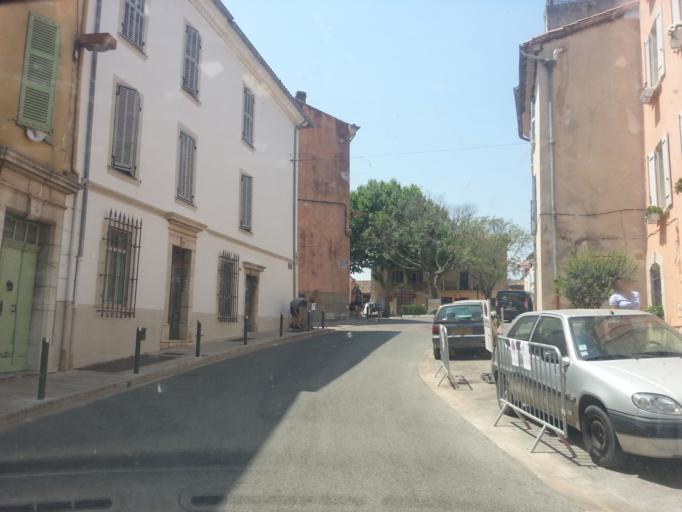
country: FR
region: Provence-Alpes-Cote d'Azur
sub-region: Departement du Var
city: Flassans-sur-Issole
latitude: 43.3683
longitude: 6.2208
